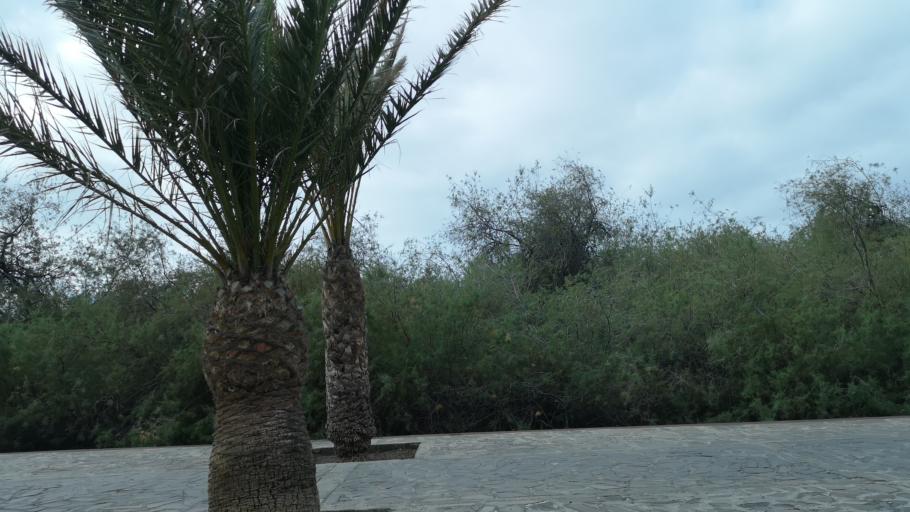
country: ES
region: Canary Islands
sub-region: Provincia de Santa Cruz de Tenerife
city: Alajero
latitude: 28.0849
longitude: -17.3367
